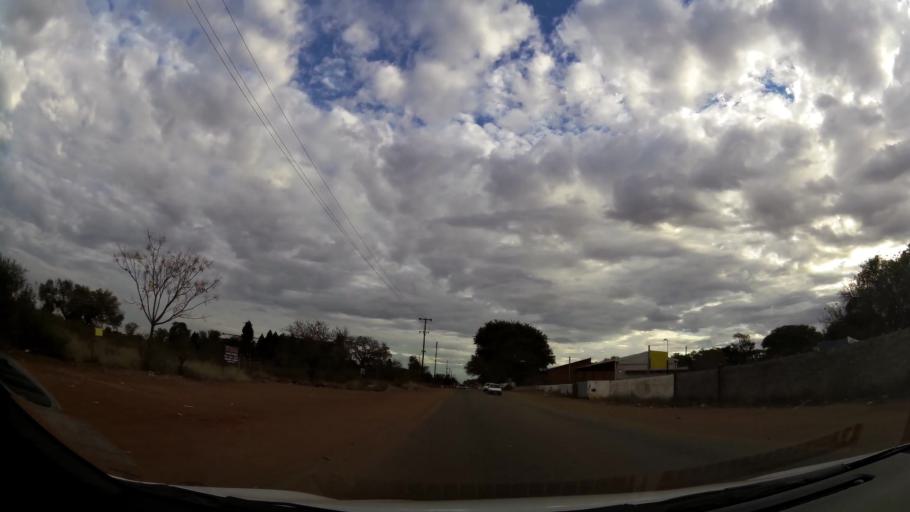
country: ZA
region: Limpopo
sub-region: Waterberg District Municipality
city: Modimolle
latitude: -24.5185
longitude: 28.7189
